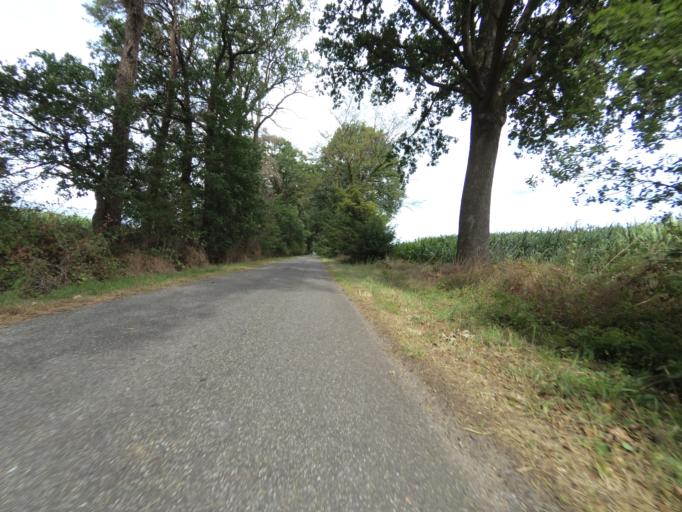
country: DE
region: North Rhine-Westphalia
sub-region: Regierungsbezirk Munster
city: Ahaus
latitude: 52.1263
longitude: 7.0048
